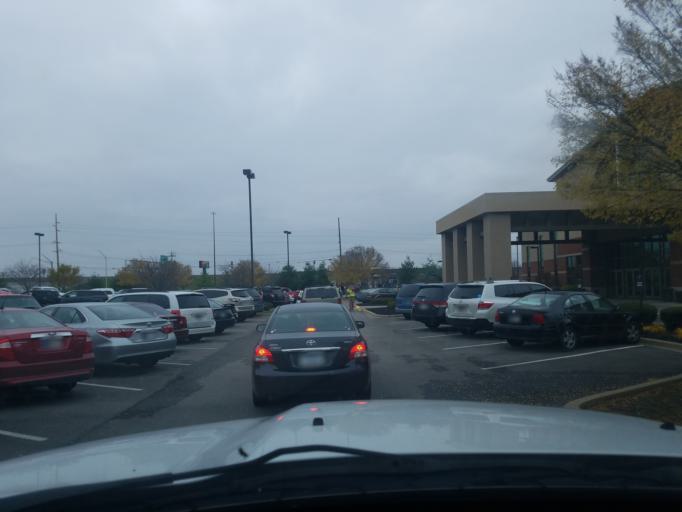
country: US
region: Indiana
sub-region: Clark County
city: Clarksville
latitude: 38.3213
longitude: -85.7499
